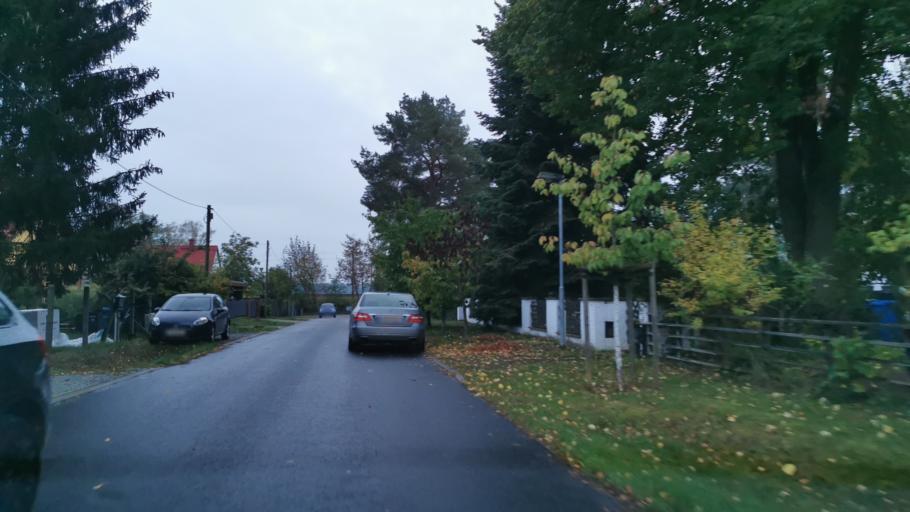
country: DE
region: Brandenburg
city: Michendorf
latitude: 52.3248
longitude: 13.0690
